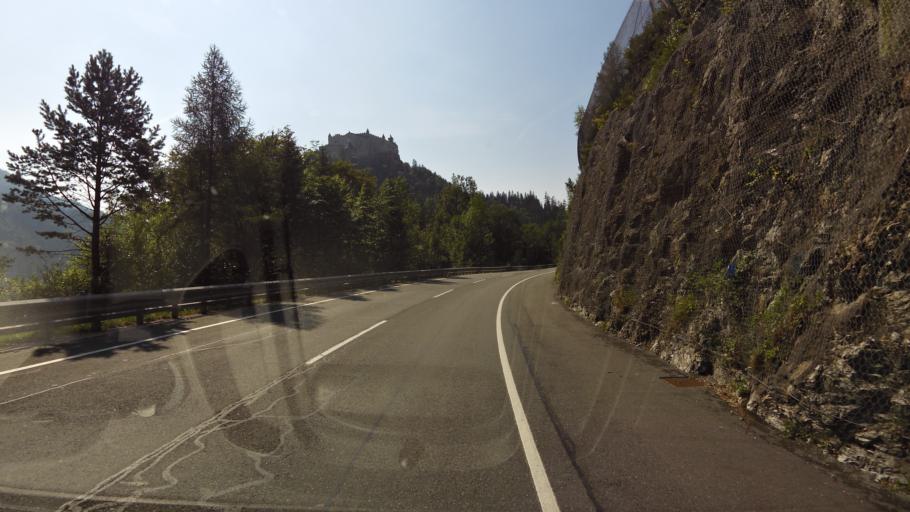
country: AT
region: Salzburg
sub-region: Politischer Bezirk Sankt Johann im Pongau
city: Werfen
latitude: 47.4862
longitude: 13.1853
